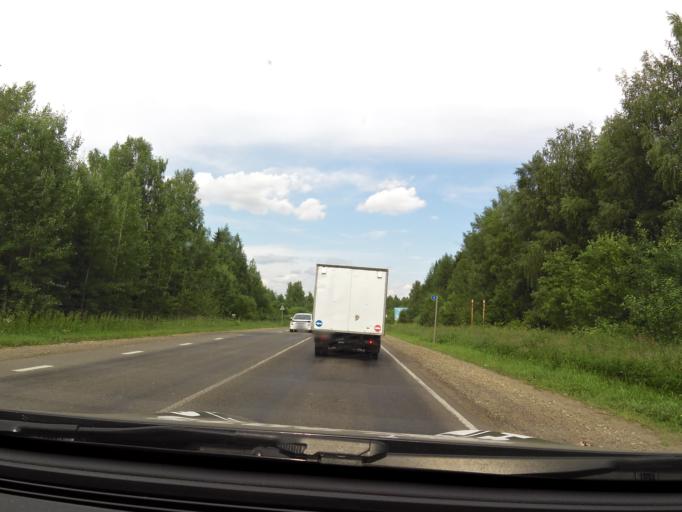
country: RU
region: Kirov
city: Vakhrushi
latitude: 58.6981
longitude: 50.0862
